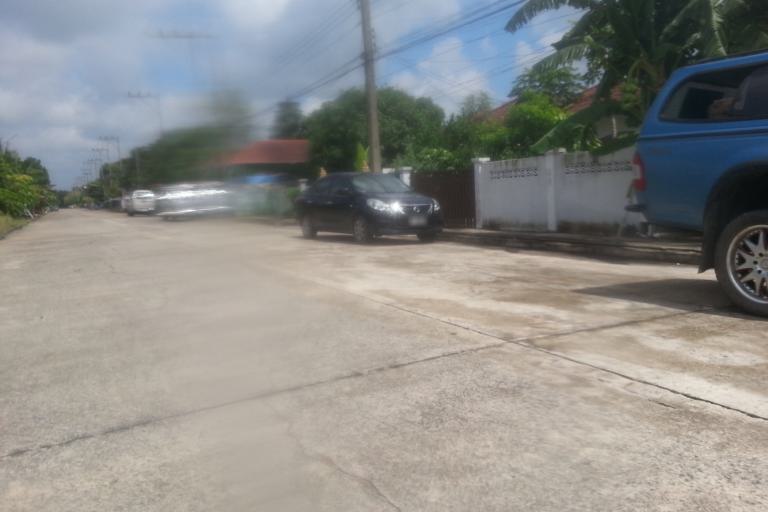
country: TH
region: Pathum Thani
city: Nong Suea
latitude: 14.0479
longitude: 100.8632
